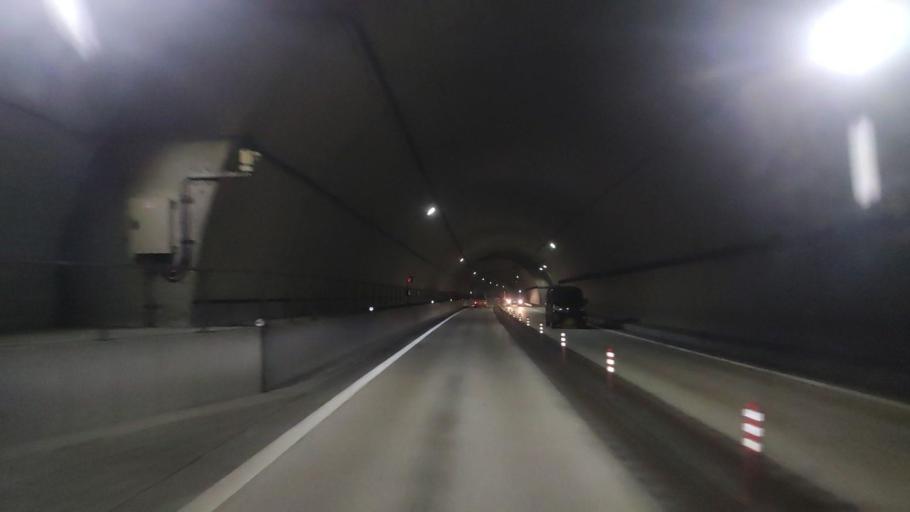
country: JP
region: Wakayama
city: Tanabe
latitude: 33.5891
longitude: 135.4419
